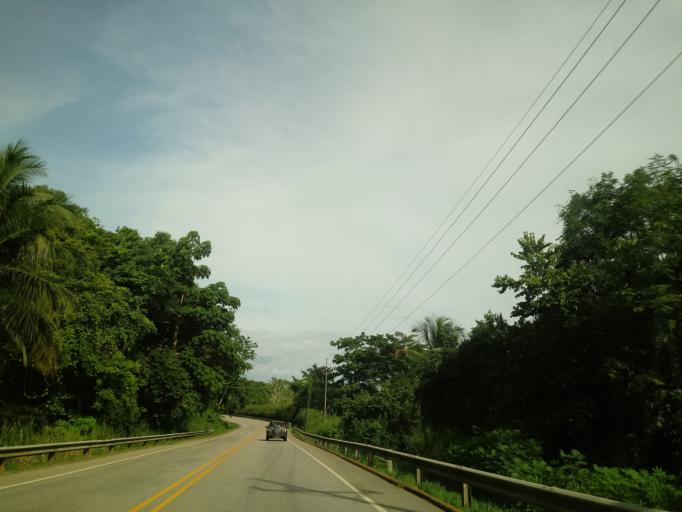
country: CR
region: San Jose
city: Daniel Flores
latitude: 9.2068
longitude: -83.8012
